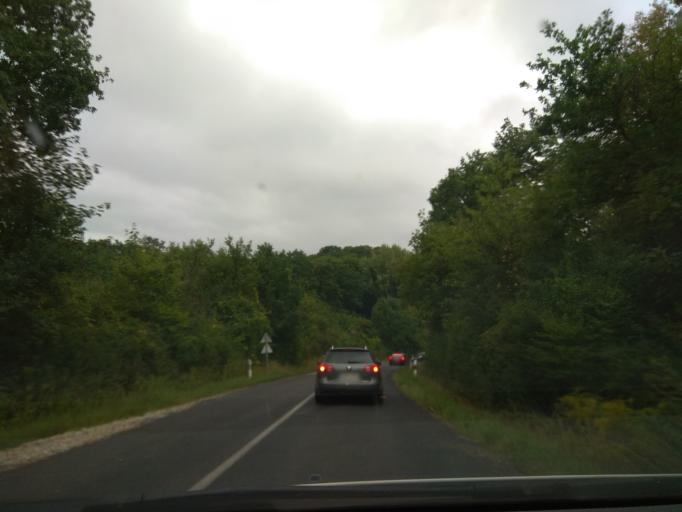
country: HU
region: Borsod-Abauj-Zemplen
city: Harsany
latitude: 48.0144
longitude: 20.7639
